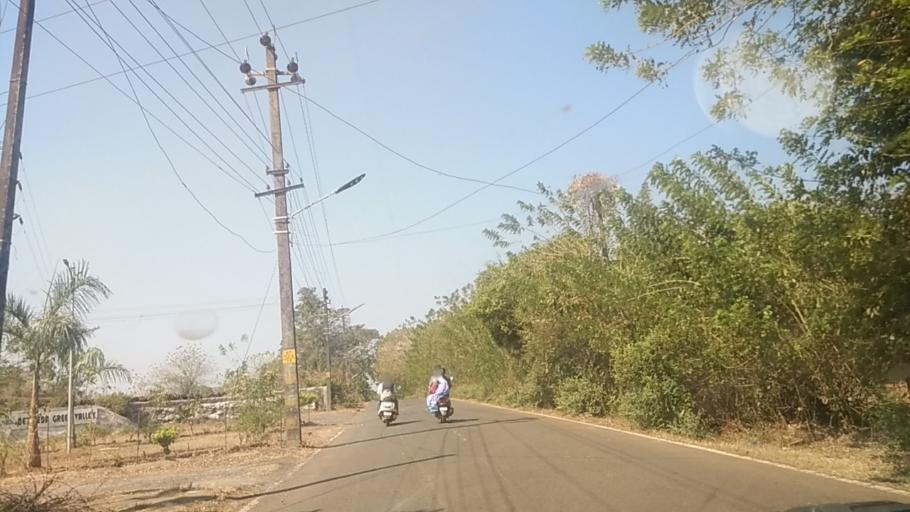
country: IN
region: Goa
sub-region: North Goa
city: Queula
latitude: 15.3434
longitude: 74.0133
